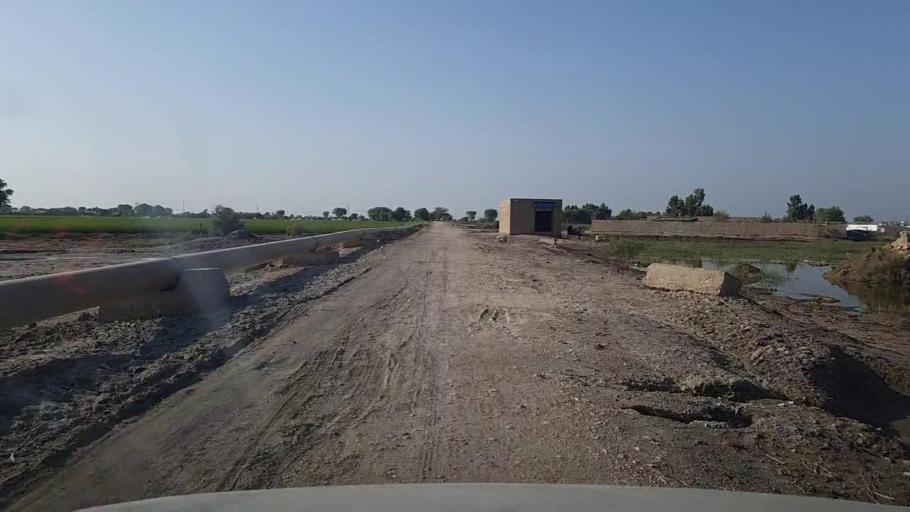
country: PK
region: Sindh
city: Kandhkot
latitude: 28.2853
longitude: 69.3339
